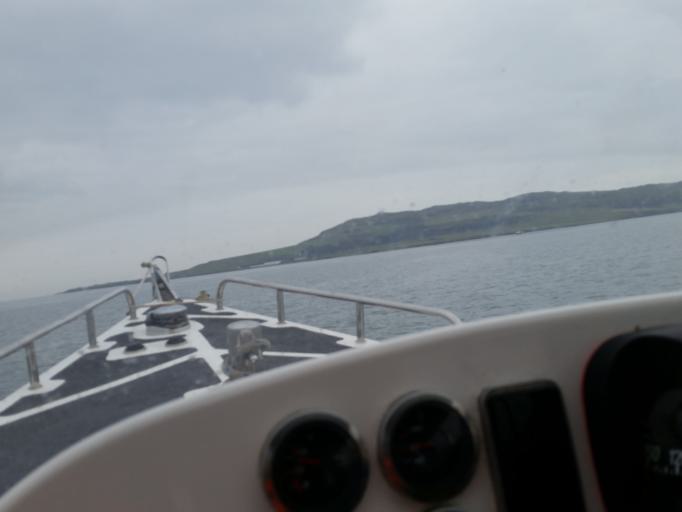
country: IE
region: Leinster
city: Portraine
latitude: 53.4865
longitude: -6.0495
